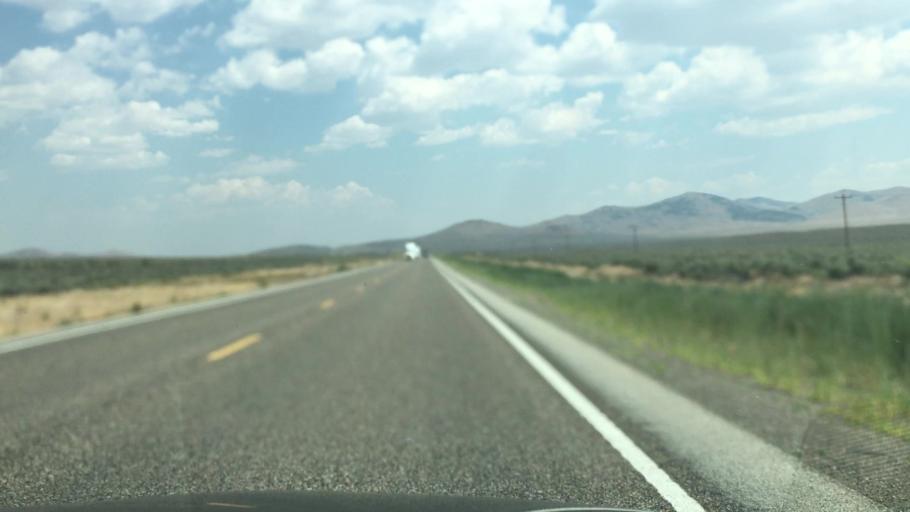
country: US
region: Nevada
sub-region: Elko County
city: Wells
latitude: 41.1510
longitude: -114.9029
